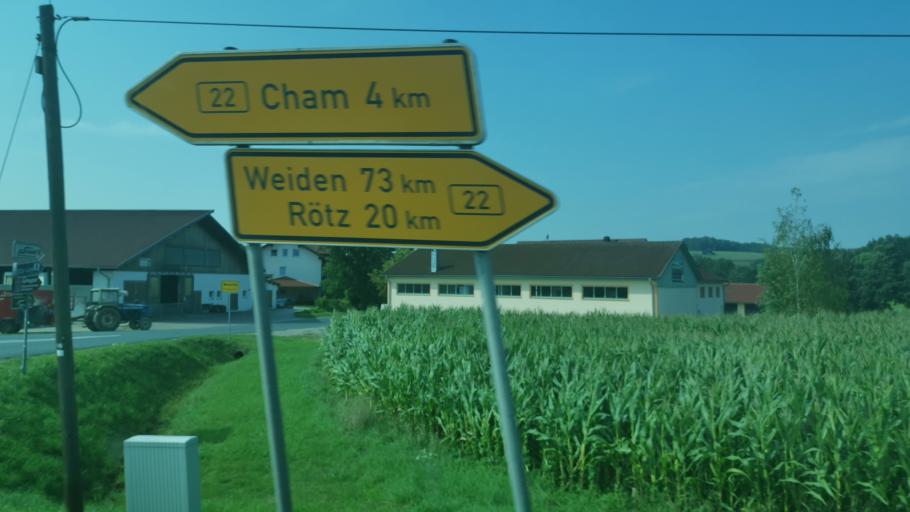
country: DE
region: Bavaria
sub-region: Upper Palatinate
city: Willmering
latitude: 49.2470
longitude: 12.6533
